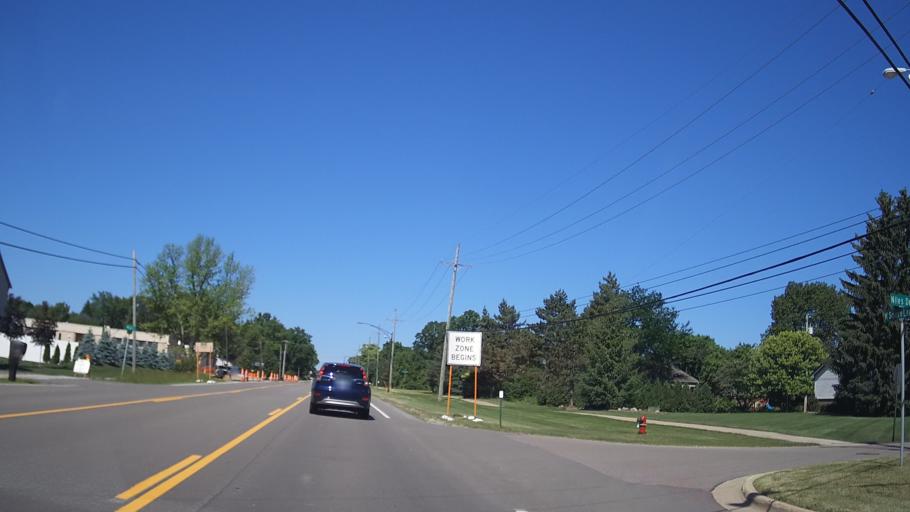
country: US
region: Michigan
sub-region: Oakland County
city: Troy
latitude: 42.6064
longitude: -83.1517
